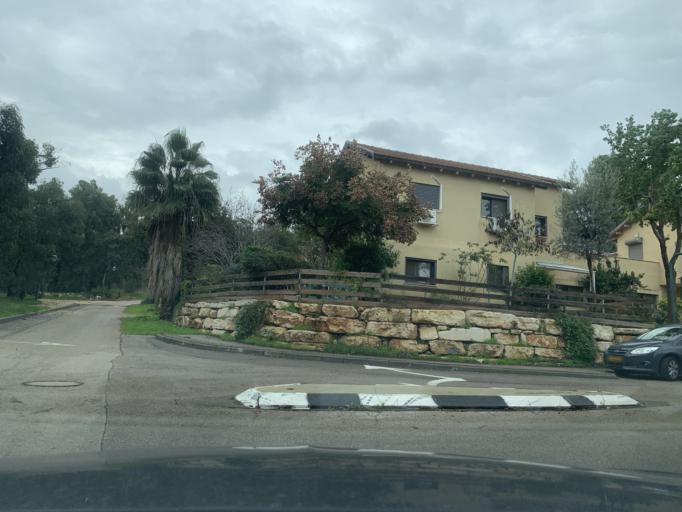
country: PS
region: West Bank
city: Qalqilyah
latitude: 32.2138
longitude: 34.9818
